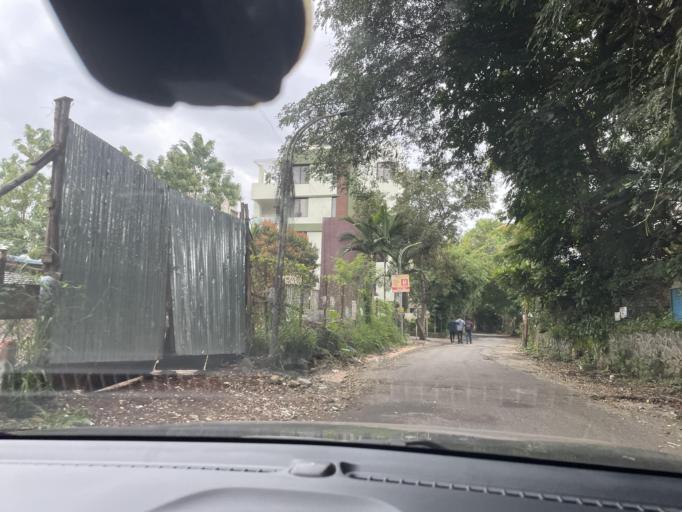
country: IN
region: Maharashtra
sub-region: Pune Division
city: Kharakvasla
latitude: 18.5140
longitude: 73.7792
